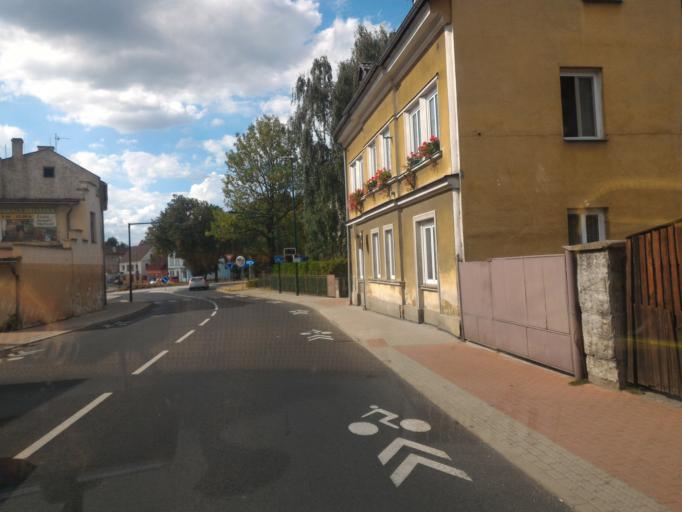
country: CZ
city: Mimon
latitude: 50.6530
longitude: 14.7332
